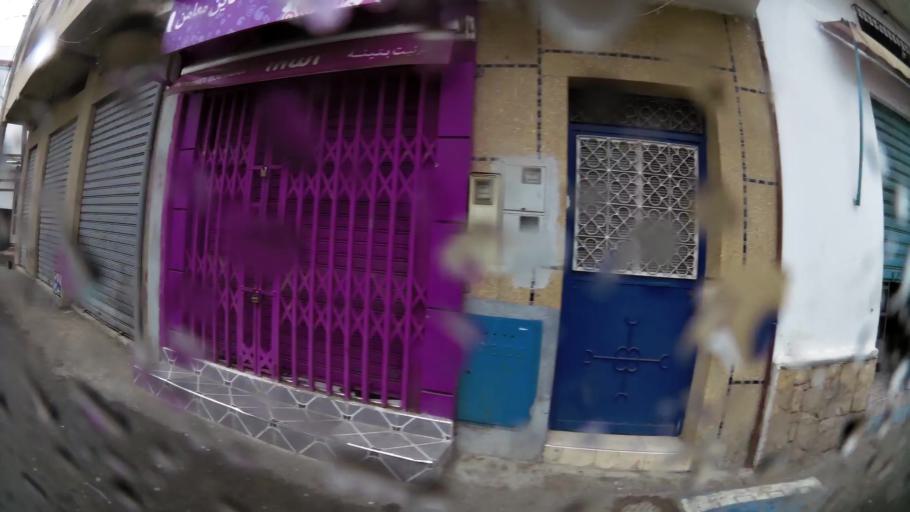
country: MA
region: Tanger-Tetouan
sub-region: Tetouan
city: Martil
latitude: 35.6194
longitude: -5.2789
